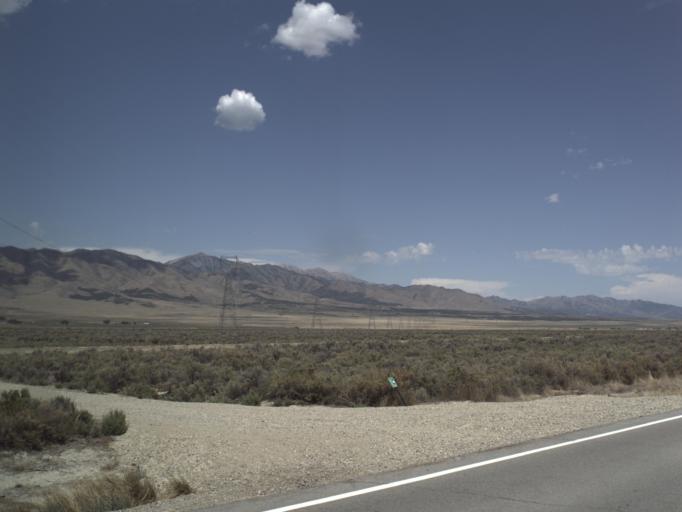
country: US
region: Utah
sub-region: Tooele County
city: Tooele
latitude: 40.3444
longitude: -112.4110
